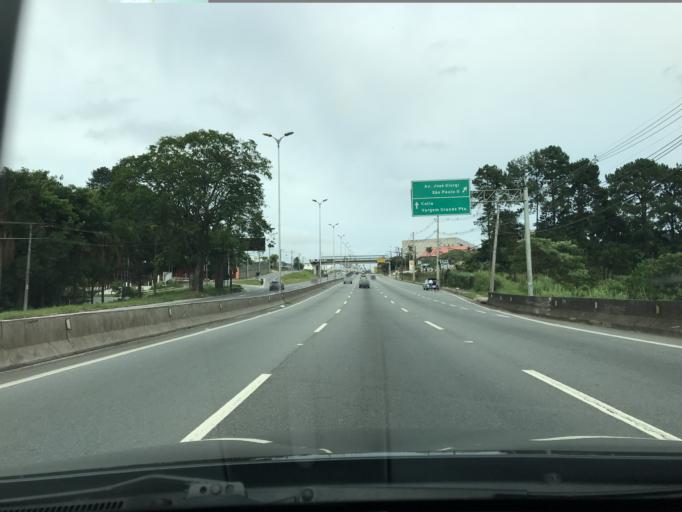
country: BR
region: Sao Paulo
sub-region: Embu
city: Embu
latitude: -23.5967
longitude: -46.8604
